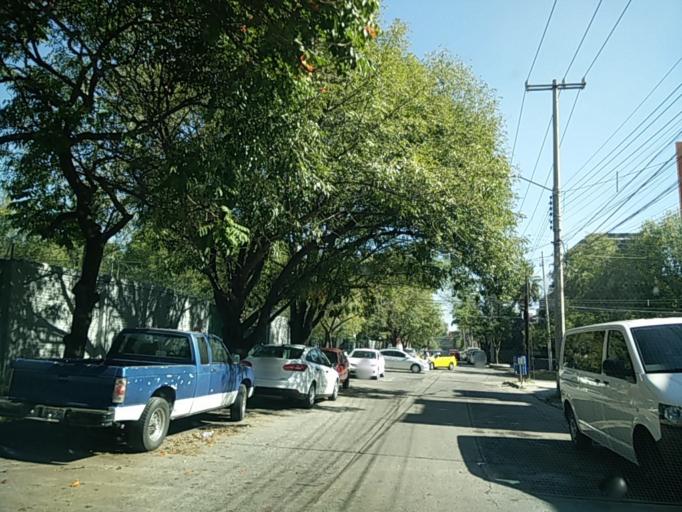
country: MX
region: Jalisco
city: Guadalajara
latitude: 20.6556
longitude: -103.3924
